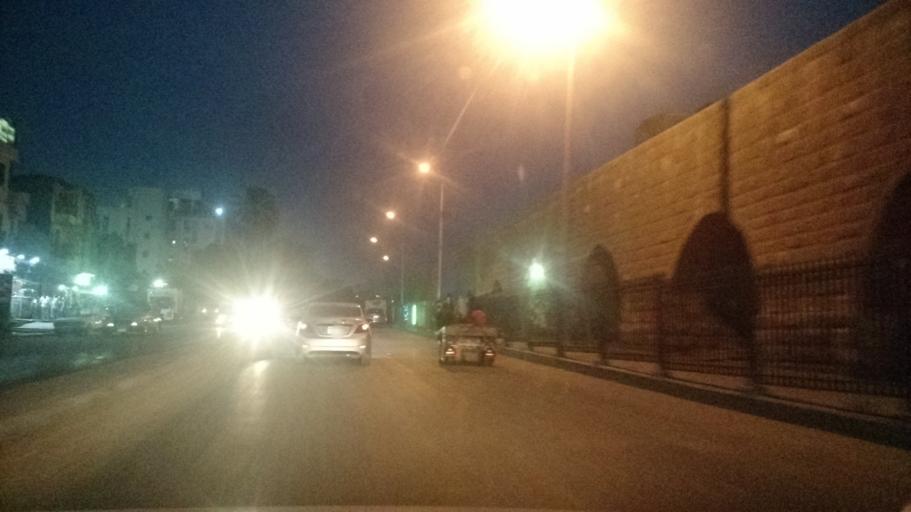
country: EG
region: Al Jizah
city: Al Jizah
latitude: 30.0208
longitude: 31.2413
